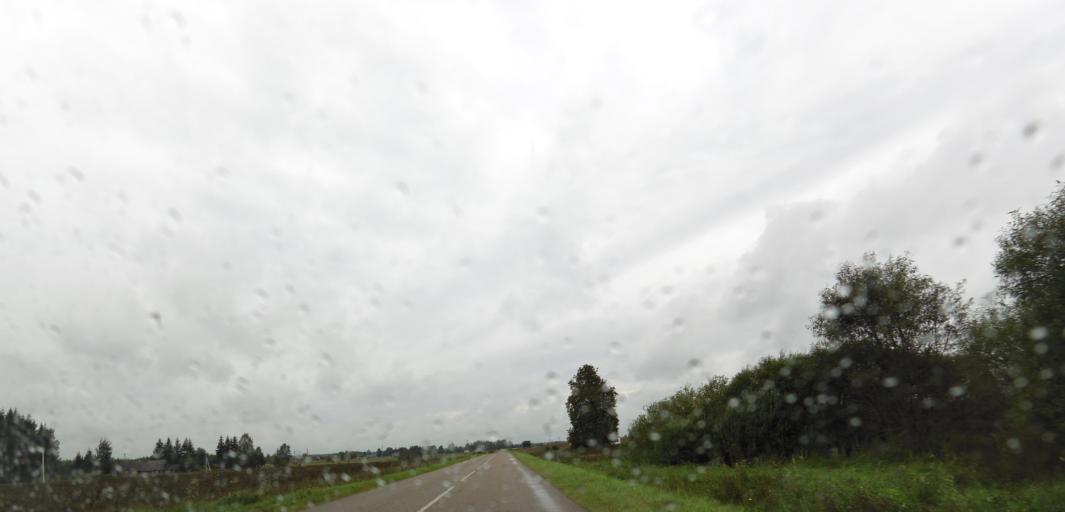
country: LT
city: Sirvintos
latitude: 55.0795
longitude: 25.0093
